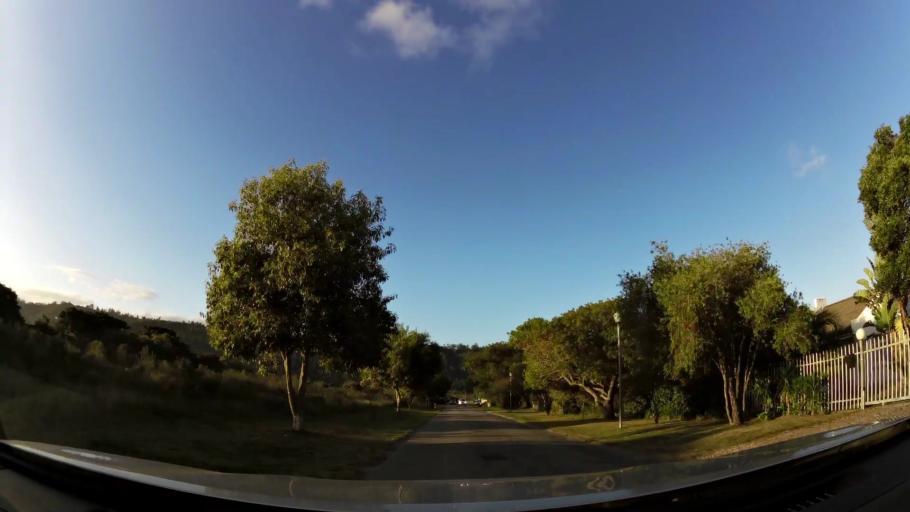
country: ZA
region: Western Cape
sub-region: Eden District Municipality
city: Knysna
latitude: -34.0158
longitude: 22.7863
